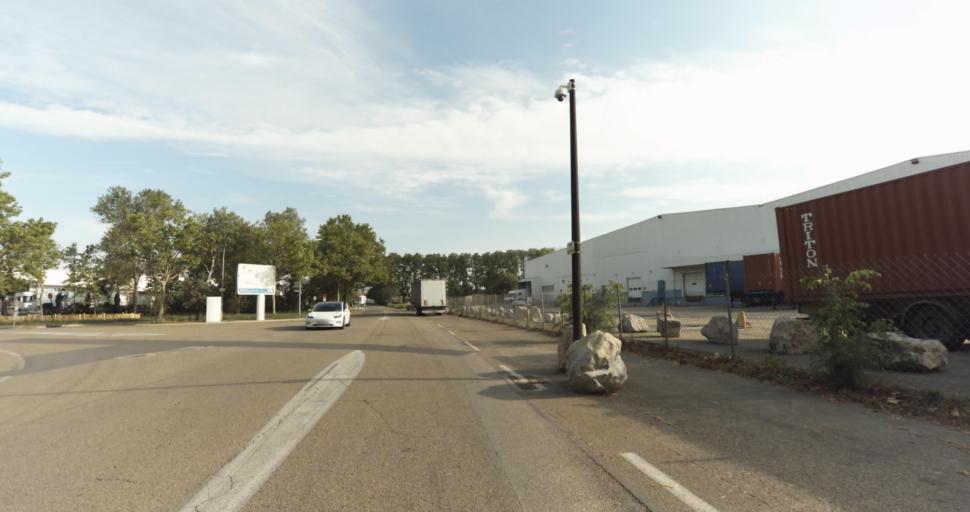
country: FR
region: Languedoc-Roussillon
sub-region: Departement du Gard
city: Rodilhan
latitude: 43.8400
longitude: 4.4168
